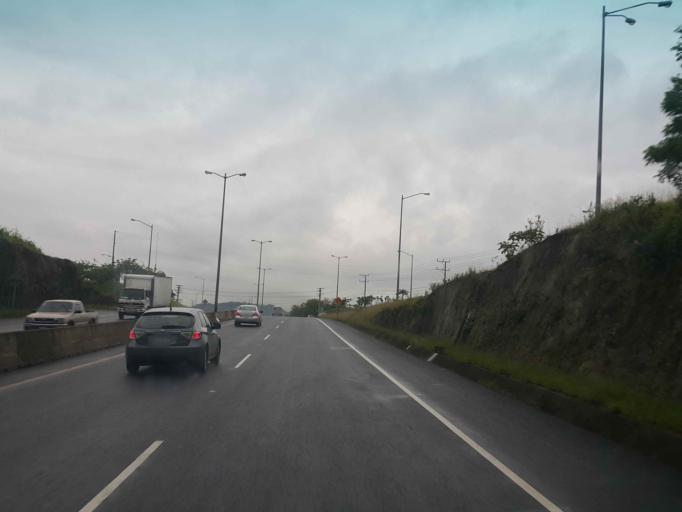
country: CR
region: Heredia
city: Colon
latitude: 9.9367
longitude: -84.2191
